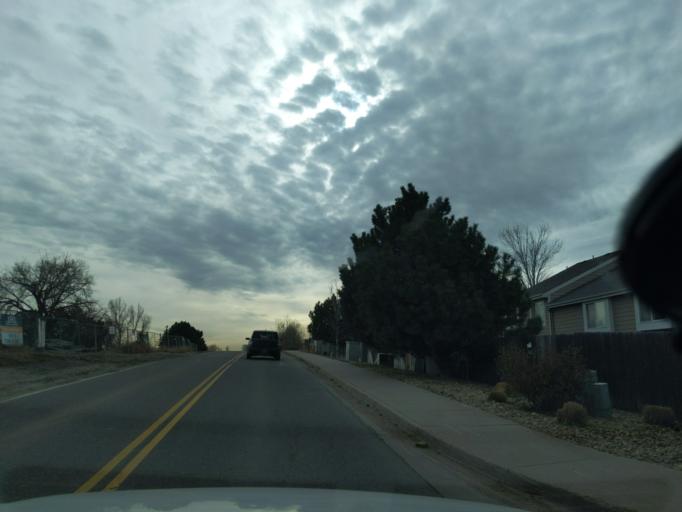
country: US
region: Colorado
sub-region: Adams County
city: Thornton
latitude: 39.8826
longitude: -104.9590
